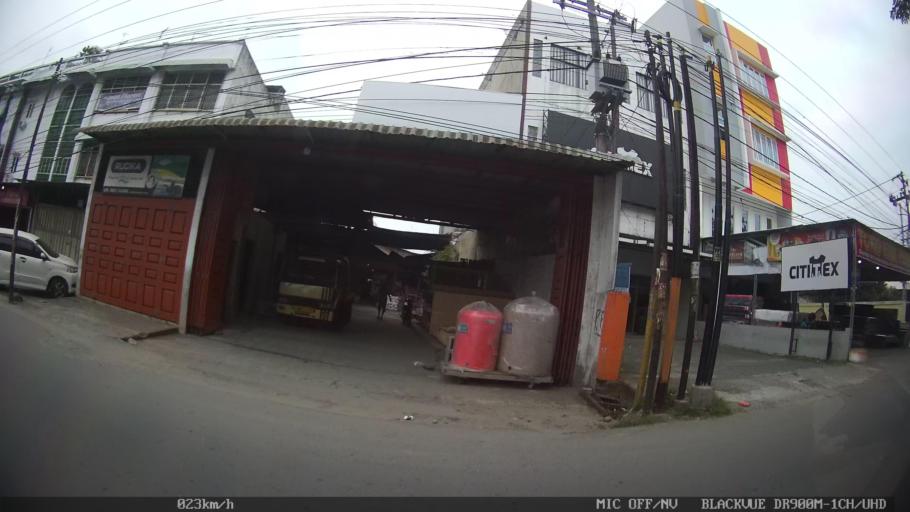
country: ID
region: North Sumatra
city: Deli Tua
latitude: 3.5405
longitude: 98.6854
